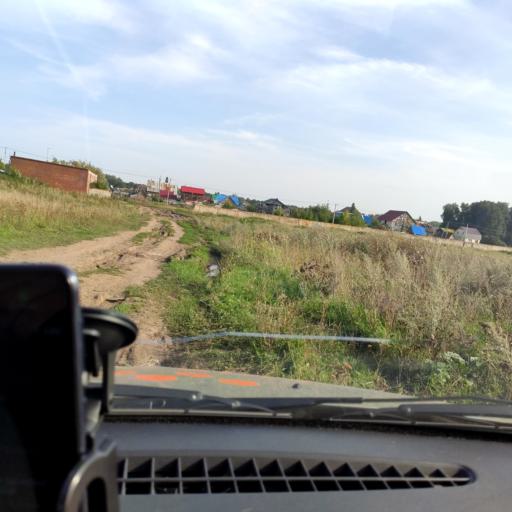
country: RU
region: Bashkortostan
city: Ufa
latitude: 54.8221
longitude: 56.1612
